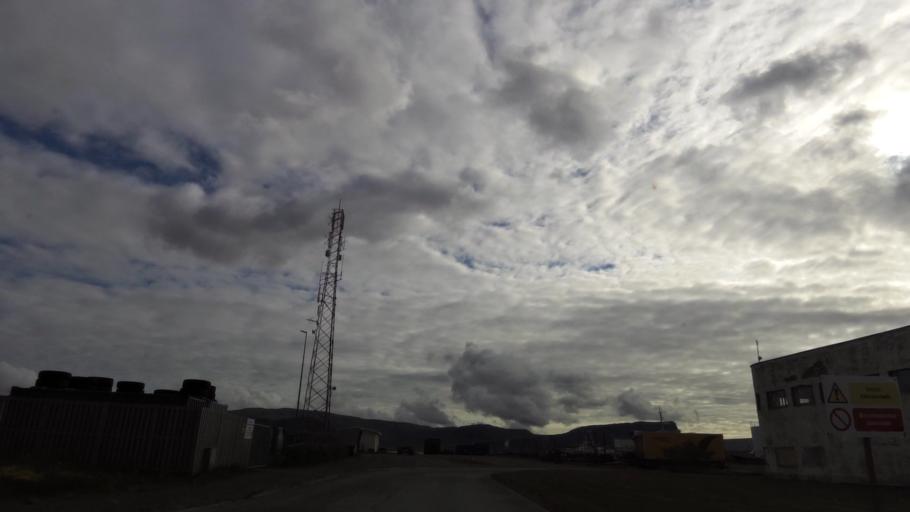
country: IS
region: West
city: Olafsvik
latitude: 65.5959
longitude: -24.0017
